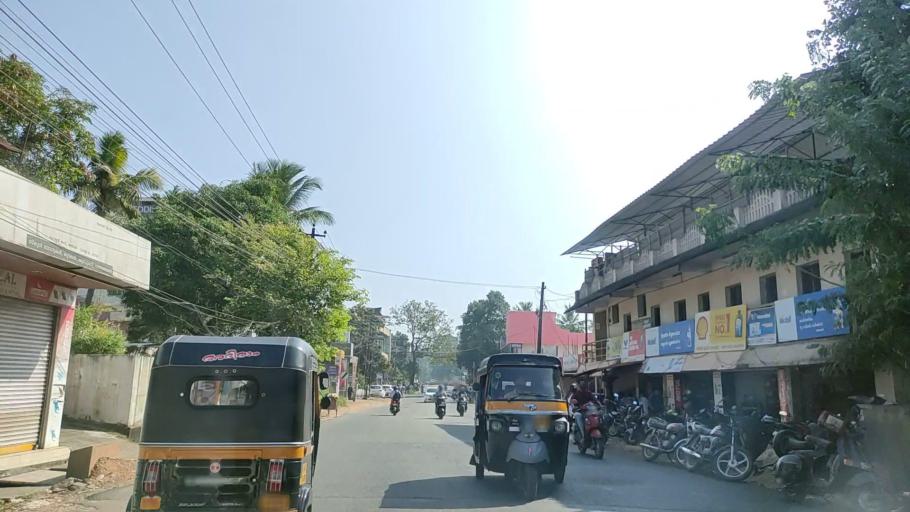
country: IN
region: Kerala
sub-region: Kollam
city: Punalur
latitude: 8.9270
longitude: 76.9208
